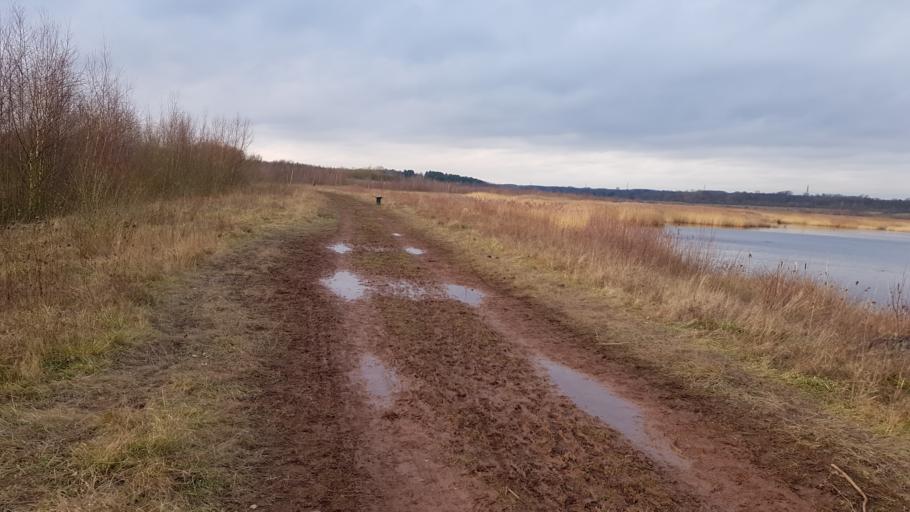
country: GB
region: England
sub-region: City and Borough of Leeds
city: Swillington
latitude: 53.7459
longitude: -1.4166
